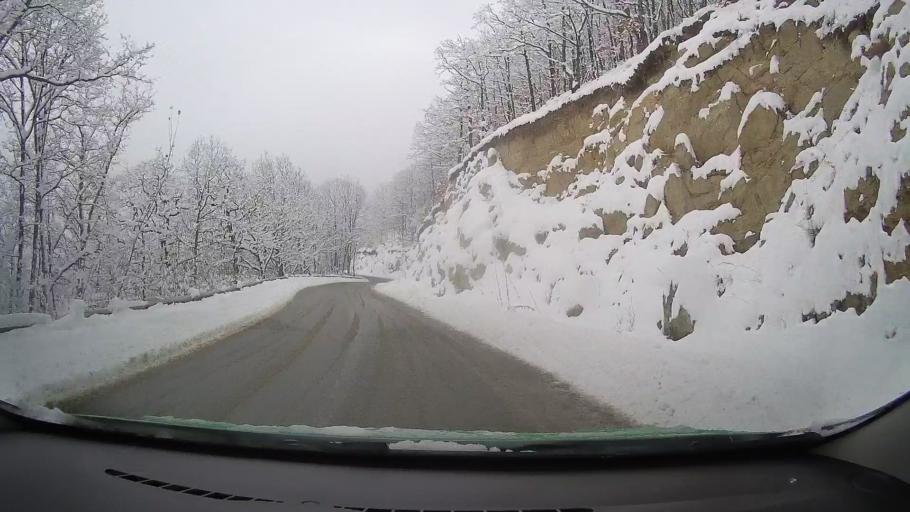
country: RO
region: Alba
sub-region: Comuna Sugag
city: Dobra
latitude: 45.7627
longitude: 23.6663
